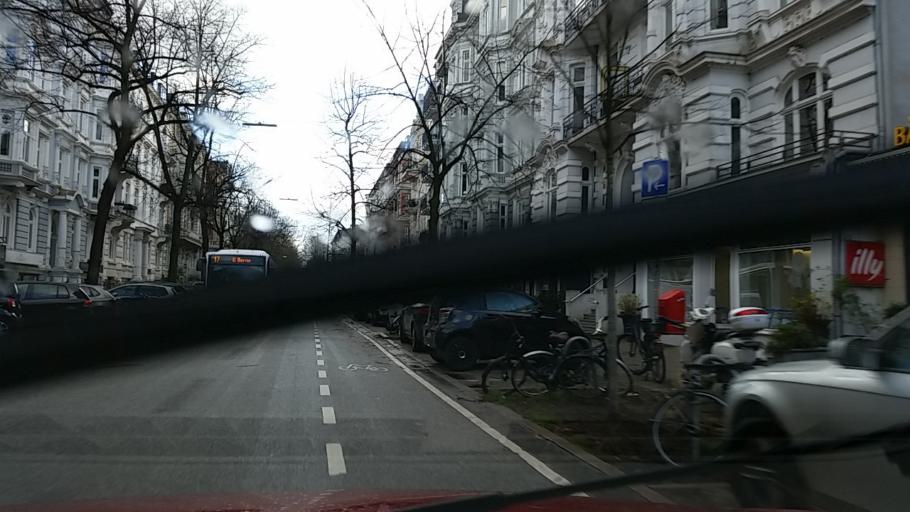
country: DE
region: Hamburg
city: Hamburg
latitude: 53.5674
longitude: 10.0187
